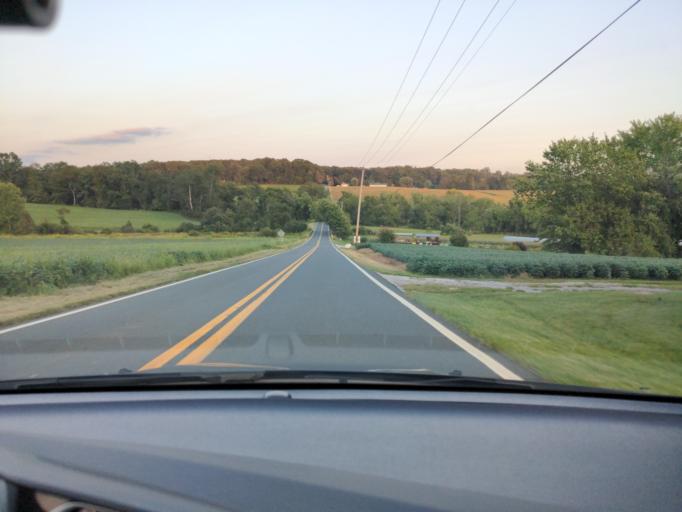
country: US
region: Maryland
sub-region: Carroll County
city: Hampstead
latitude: 39.5692
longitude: -76.8686
